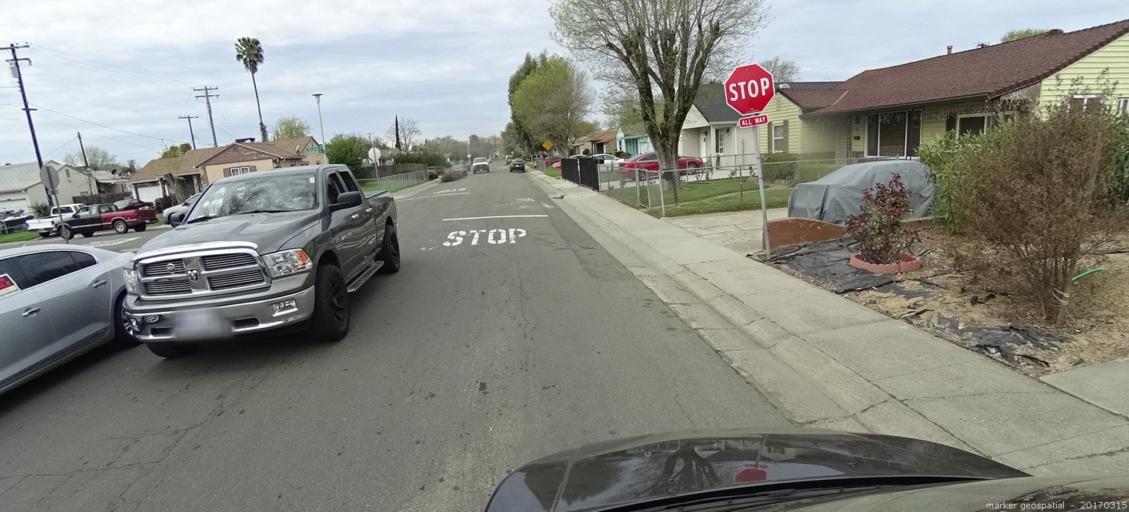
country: US
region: California
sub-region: Sacramento County
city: Parkway
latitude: 38.5171
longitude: -121.5013
